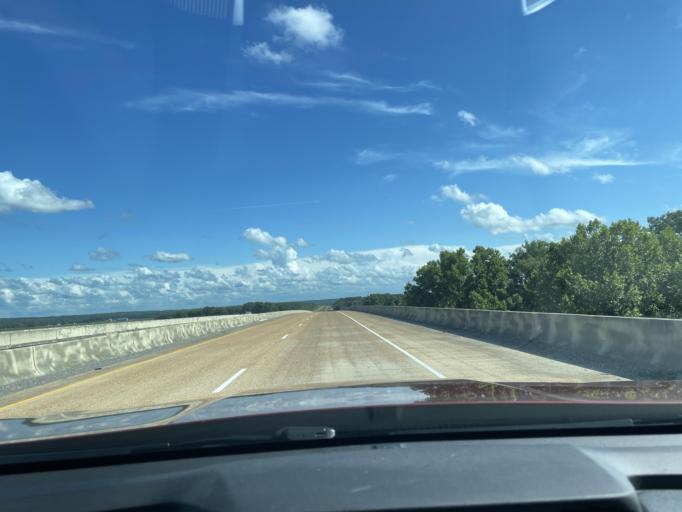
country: US
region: Mississippi
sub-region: Yazoo County
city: Yazoo City
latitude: 32.9279
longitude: -90.4127
